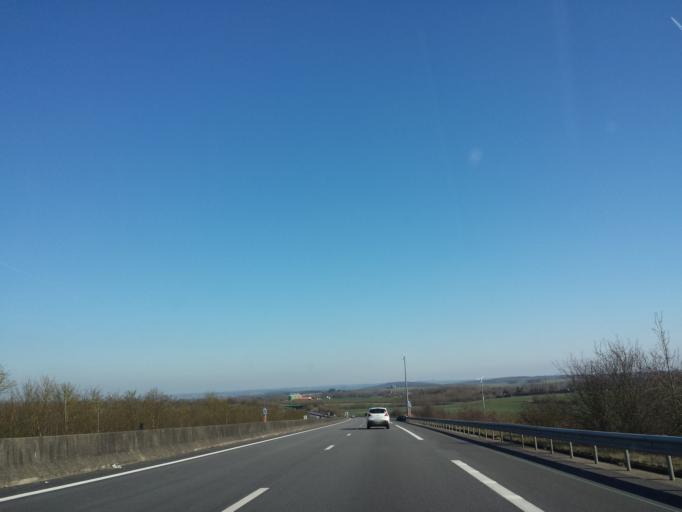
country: FR
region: Picardie
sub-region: Departement de l'Oise
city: Saint-Sulpice
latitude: 49.3296
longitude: 2.0967
